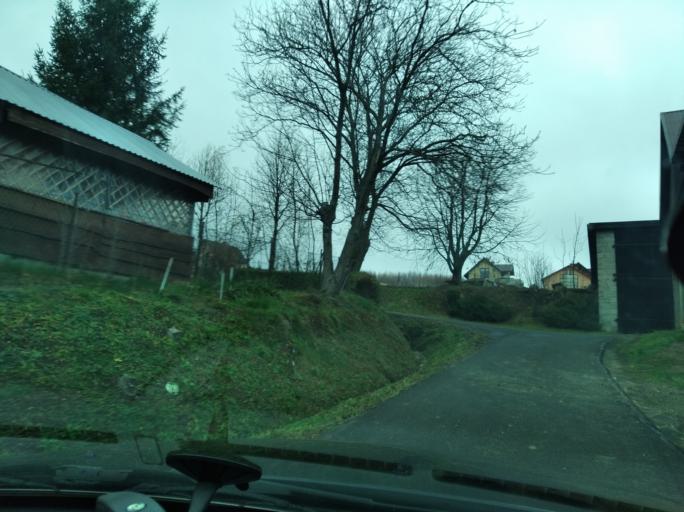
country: PL
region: Subcarpathian Voivodeship
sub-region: Powiat przeworski
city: Jawornik Polski
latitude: 49.8899
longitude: 22.2781
